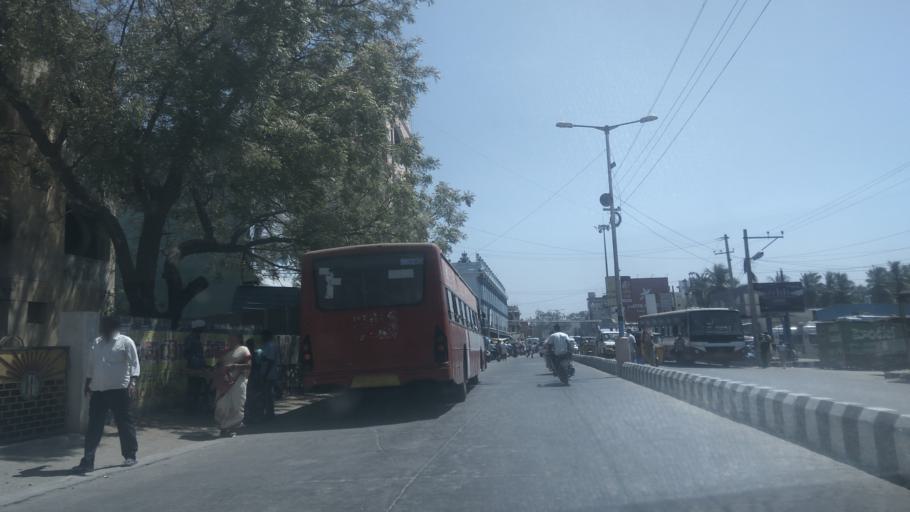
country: IN
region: Andhra Pradesh
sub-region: Chittoor
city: Tirupati
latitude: 13.6072
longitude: 79.4488
